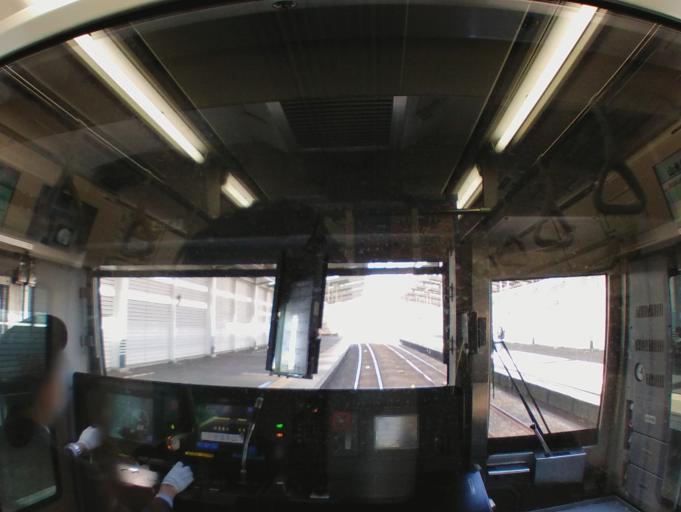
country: JP
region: Tokyo
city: Hino
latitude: 35.6293
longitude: 139.4499
